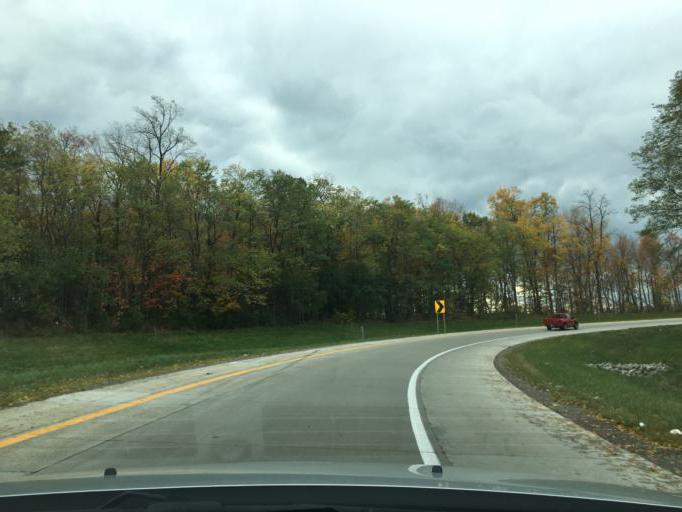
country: US
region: Michigan
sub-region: Oakland County
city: Novi
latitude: 42.4772
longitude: -83.4266
